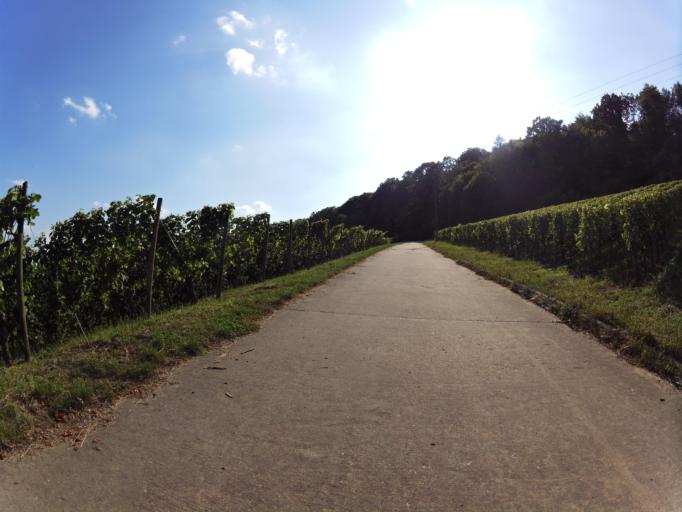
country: DE
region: Bavaria
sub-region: Regierungsbezirk Unterfranken
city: Nordheim
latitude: 49.8550
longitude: 10.1653
